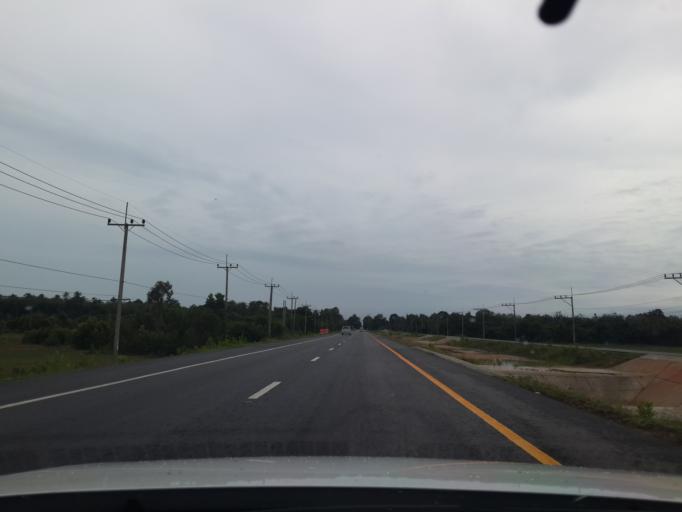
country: TH
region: Songkhla
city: Thepha
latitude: 6.8511
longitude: 100.9740
